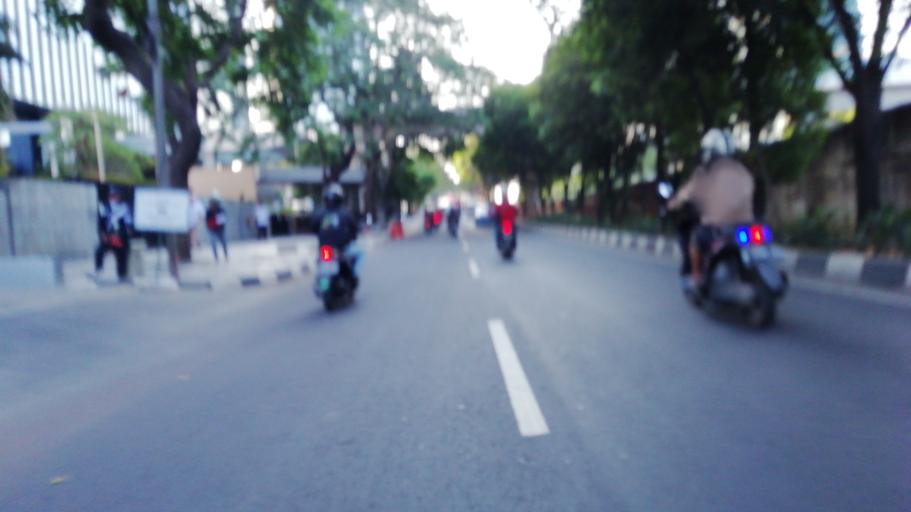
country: ID
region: Jakarta Raya
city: Jakarta
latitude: -6.3002
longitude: 106.8337
